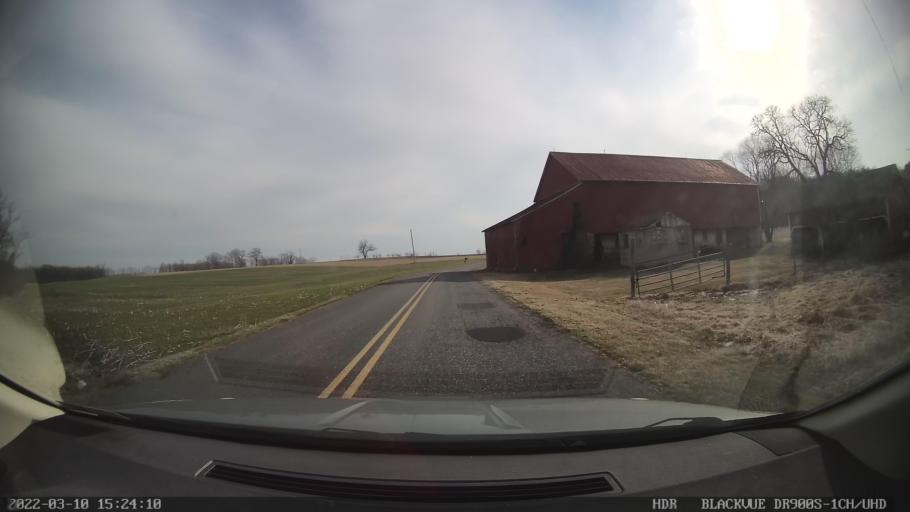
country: US
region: Pennsylvania
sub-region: Berks County
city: Oley
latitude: 40.3655
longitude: -75.7877
